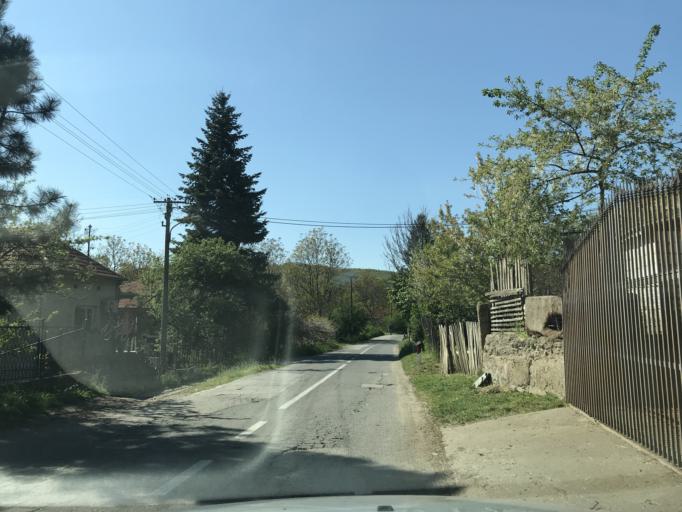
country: RS
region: Central Serbia
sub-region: Nisavski Okrug
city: Nis
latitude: 43.4085
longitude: 21.8205
